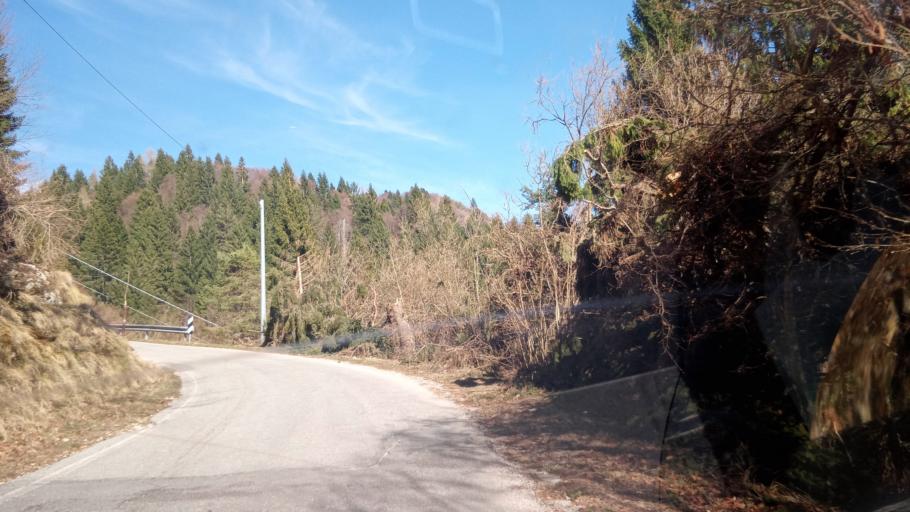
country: IT
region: Veneto
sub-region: Provincia di Treviso
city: Borso del Grappa
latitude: 45.8388
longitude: 11.7800
